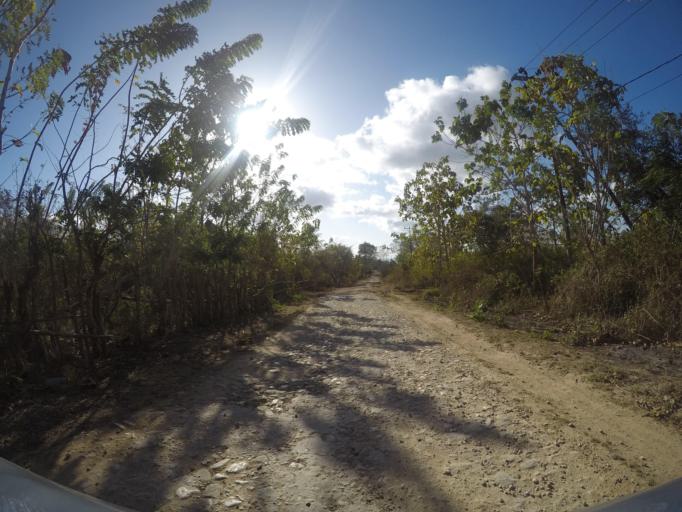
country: TL
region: Lautem
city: Lospalos
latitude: -8.4430
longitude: 126.8648
